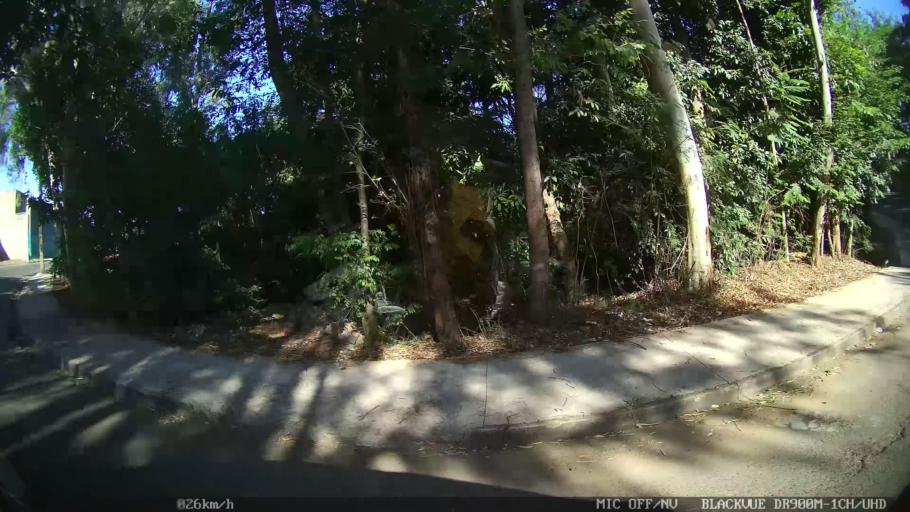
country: BR
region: Sao Paulo
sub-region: Franca
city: Franca
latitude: -20.4926
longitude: -47.4138
